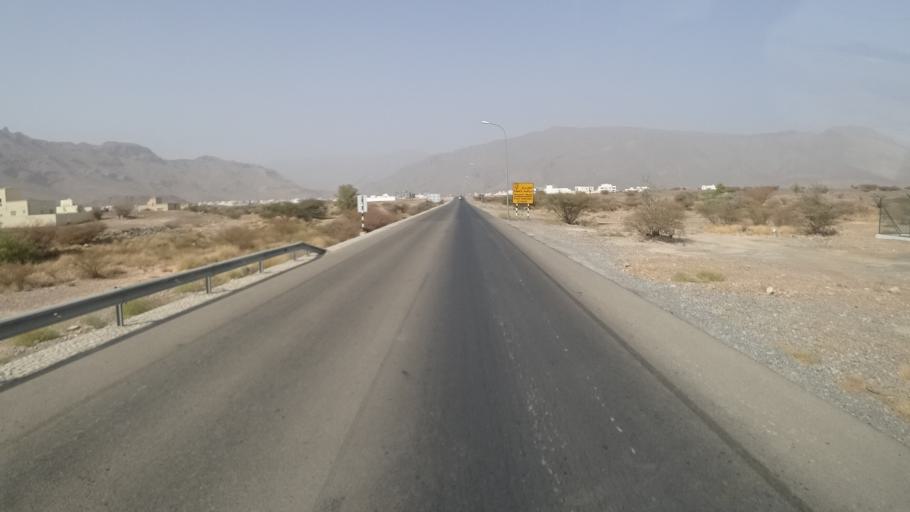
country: OM
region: Muhafazat ad Dakhiliyah
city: Nizwa
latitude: 22.9062
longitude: 57.5831
